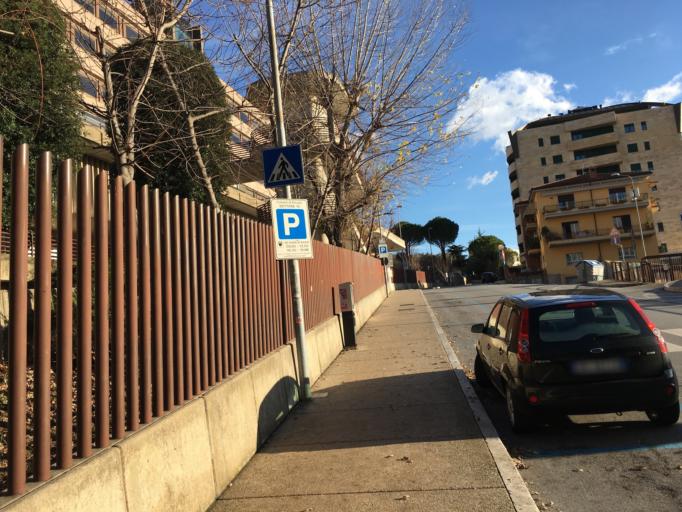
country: IT
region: Umbria
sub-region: Provincia di Perugia
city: Perugia
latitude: 43.1041
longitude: 12.3779
